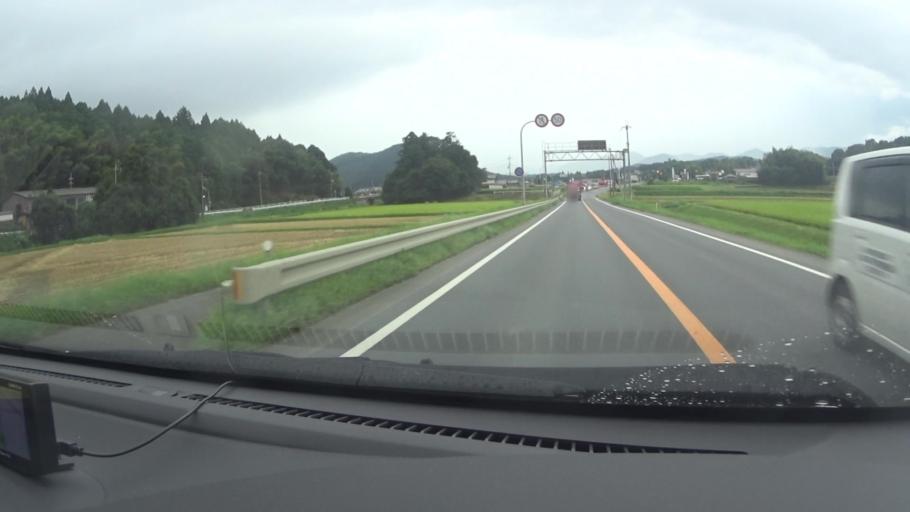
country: JP
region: Kyoto
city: Ayabe
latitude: 35.1847
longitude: 135.3666
